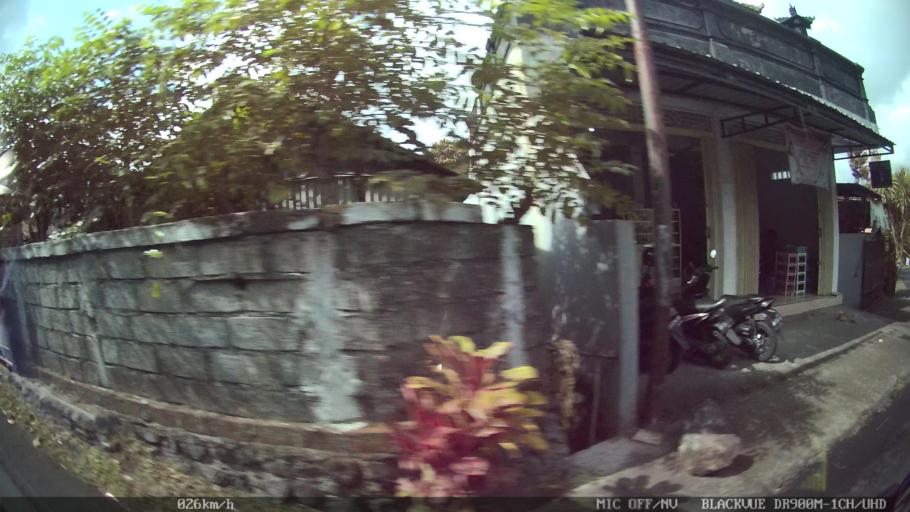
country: ID
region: Bali
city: Banjar Batur
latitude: -8.6064
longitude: 115.2050
